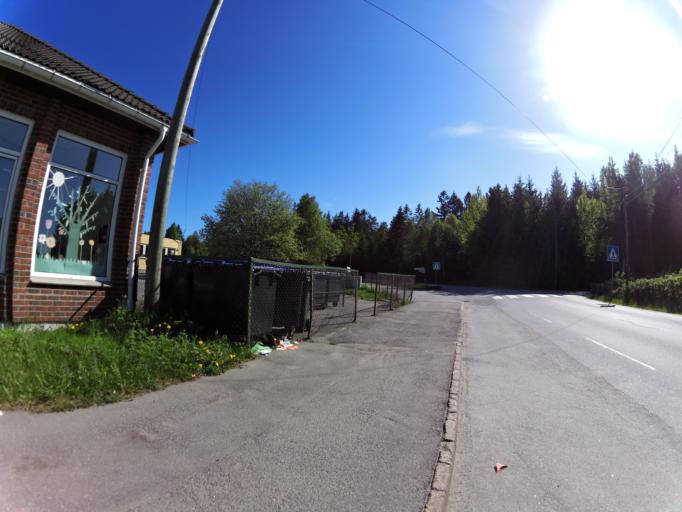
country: NO
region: Ostfold
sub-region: Sarpsborg
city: Sarpsborg
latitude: 59.2248
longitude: 11.0458
